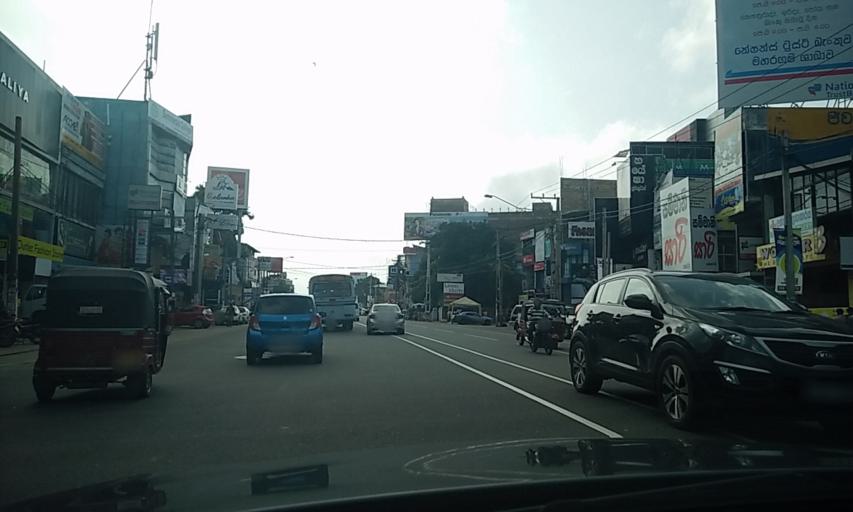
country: LK
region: Western
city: Maharagama
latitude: 6.8492
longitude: 79.9241
